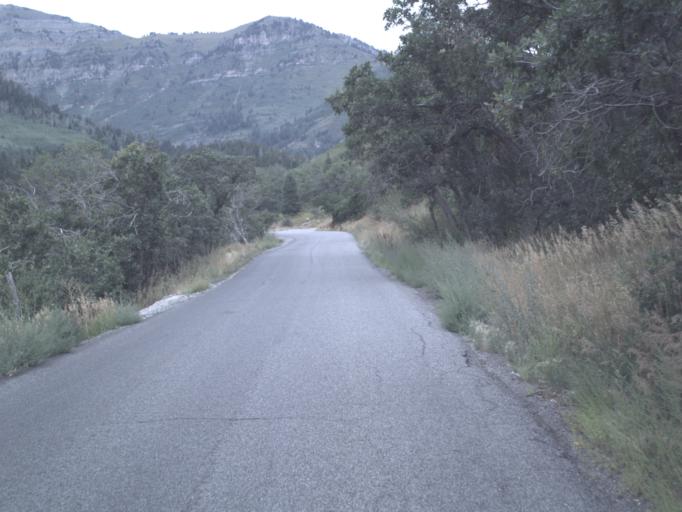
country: US
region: Utah
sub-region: Utah County
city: Lindon
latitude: 40.3981
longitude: -111.5892
